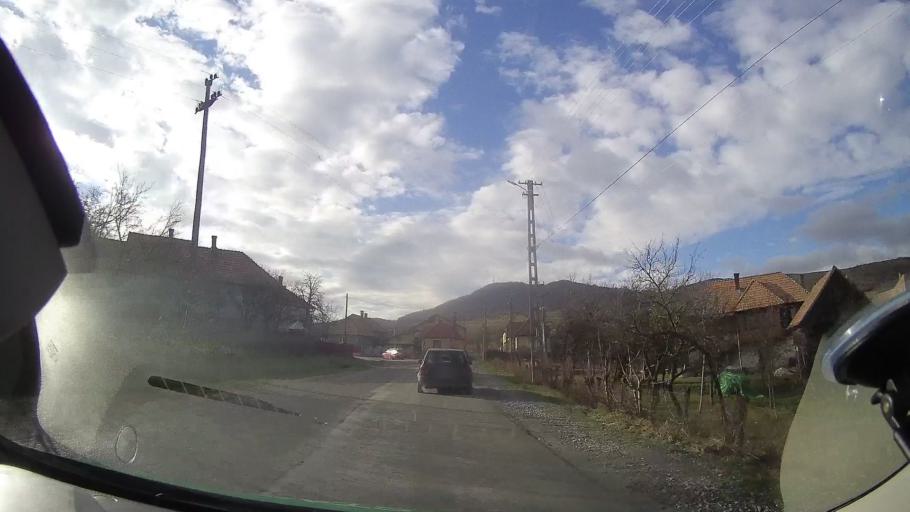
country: RO
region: Cluj
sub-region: Comuna Baisoara
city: Baisoara
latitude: 46.6199
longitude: 23.4514
